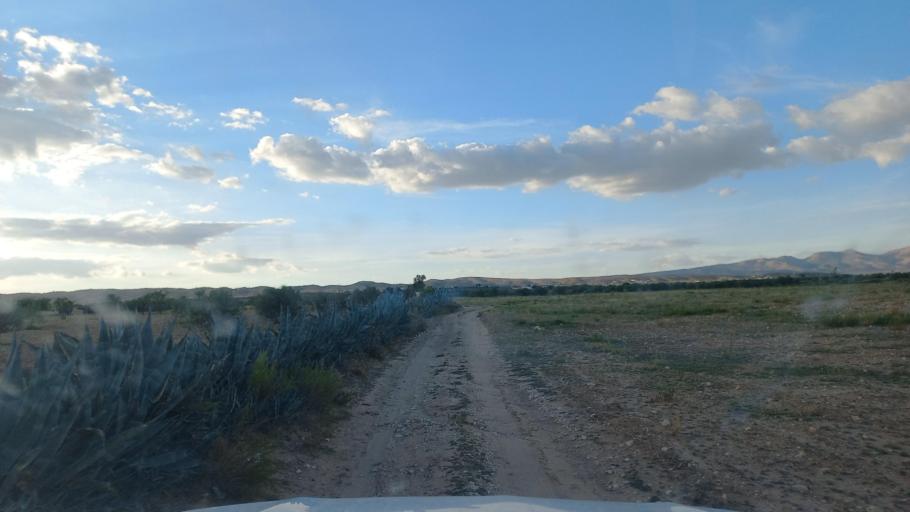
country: TN
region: Al Qasrayn
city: Sbiba
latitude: 35.3536
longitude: 9.0254
